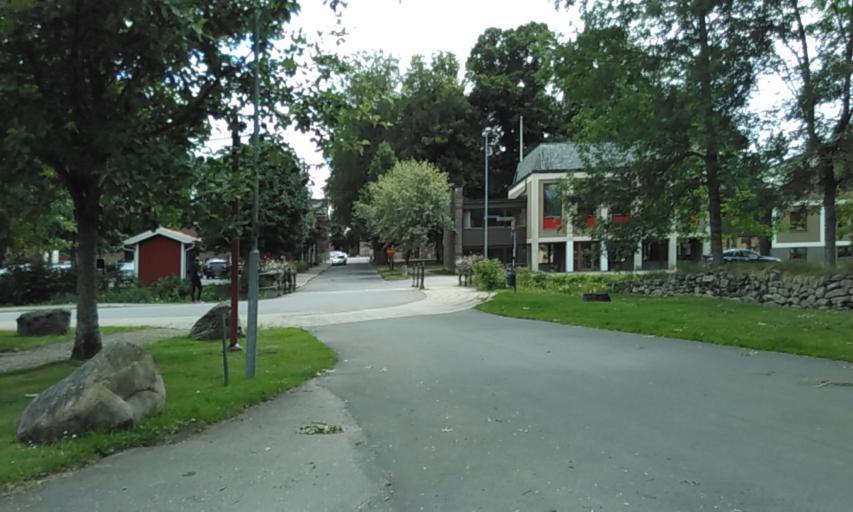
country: SE
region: Vaestra Goetaland
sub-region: Skara Kommun
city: Skara
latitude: 58.3883
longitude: 13.4396
